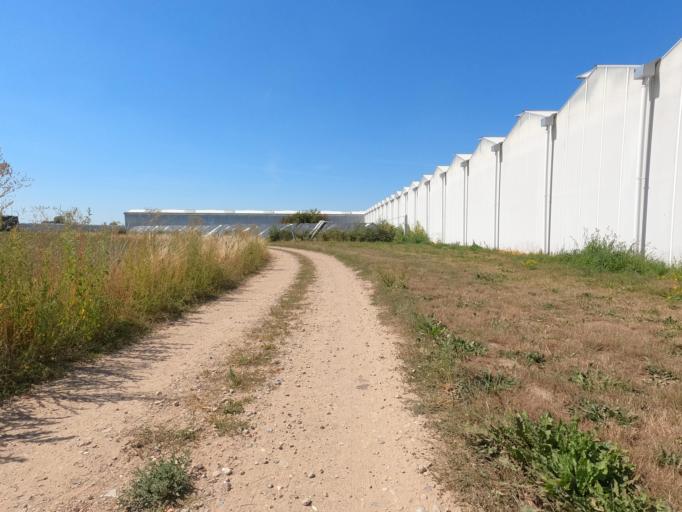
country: BE
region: Flanders
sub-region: Provincie Antwerpen
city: Wommelgem
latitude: 51.1900
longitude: 4.5248
